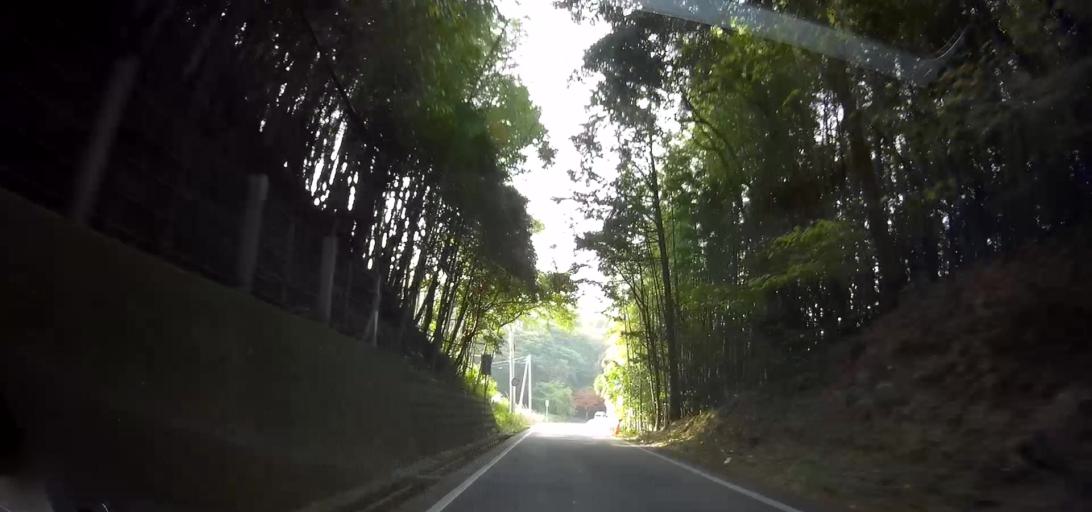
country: JP
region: Nagasaki
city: Shimabara
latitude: 32.6834
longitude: 130.1994
